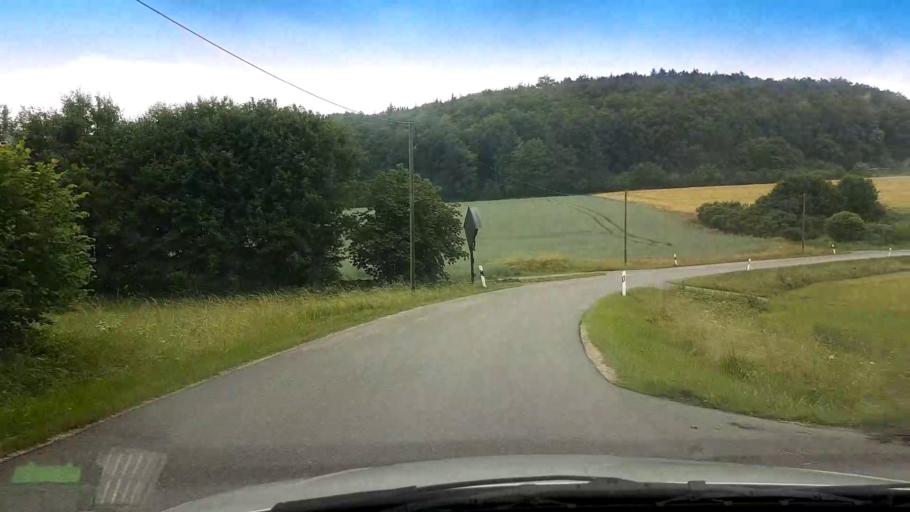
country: DE
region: Bavaria
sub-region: Upper Franconia
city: Altendorf
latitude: 50.0700
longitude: 11.1555
